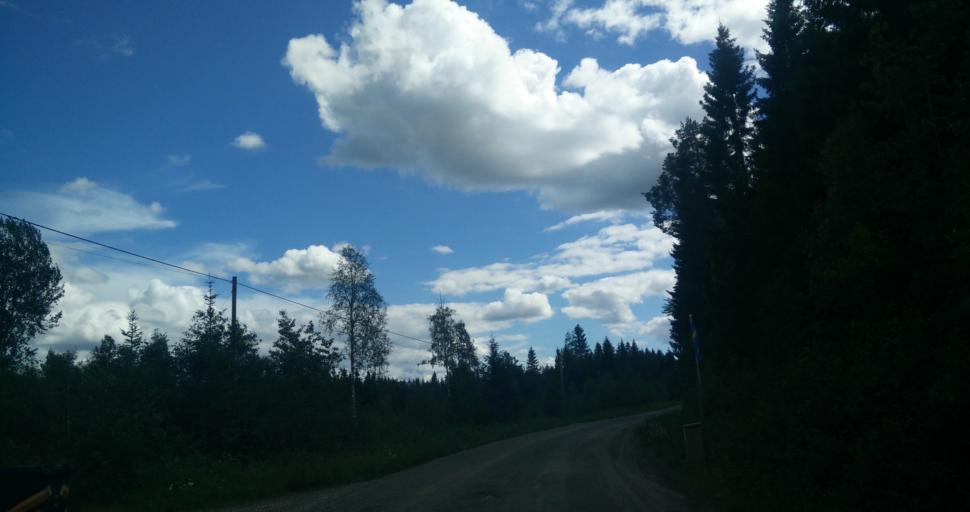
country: SE
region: Gaevleborg
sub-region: Nordanstigs Kommun
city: Bergsjoe
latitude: 62.0629
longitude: 16.7802
